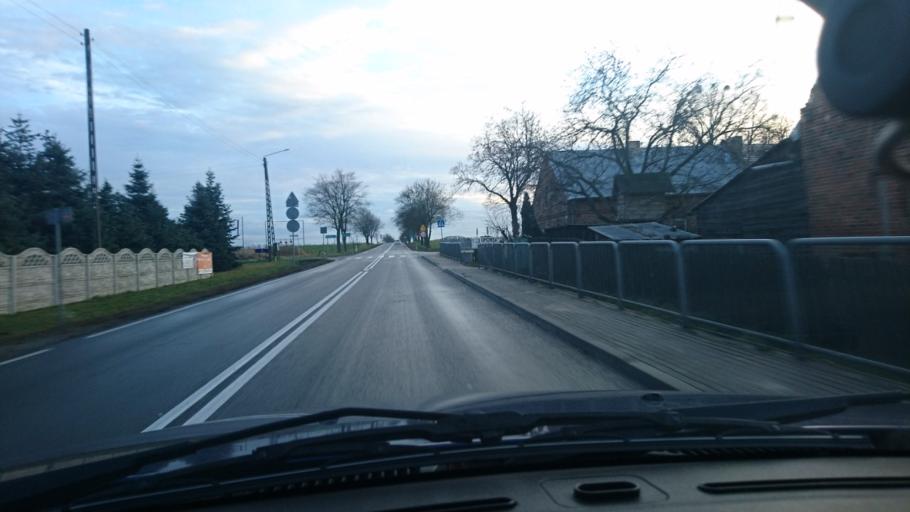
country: PL
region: Opole Voivodeship
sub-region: Powiat kluczborski
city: Byczyna
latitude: 51.0818
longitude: 18.1989
